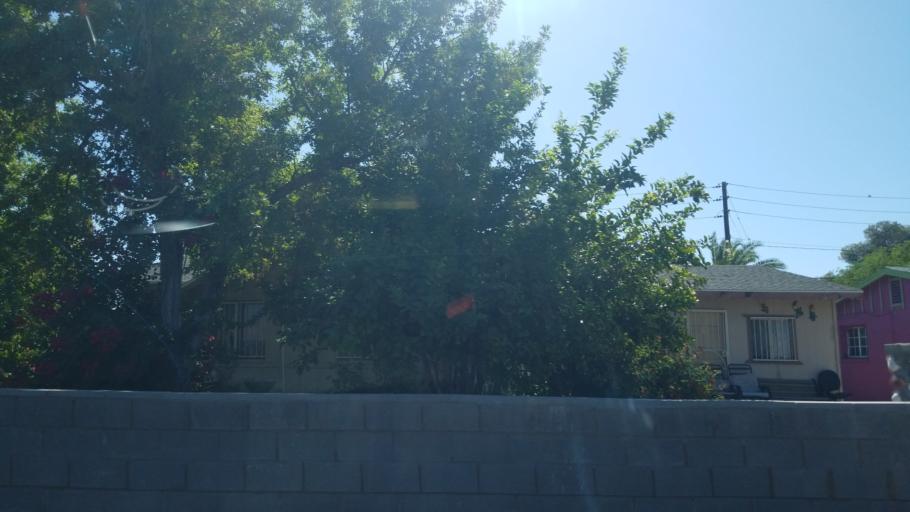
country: US
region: Arizona
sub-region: Maricopa County
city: Glendale
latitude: 33.4713
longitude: -112.1650
